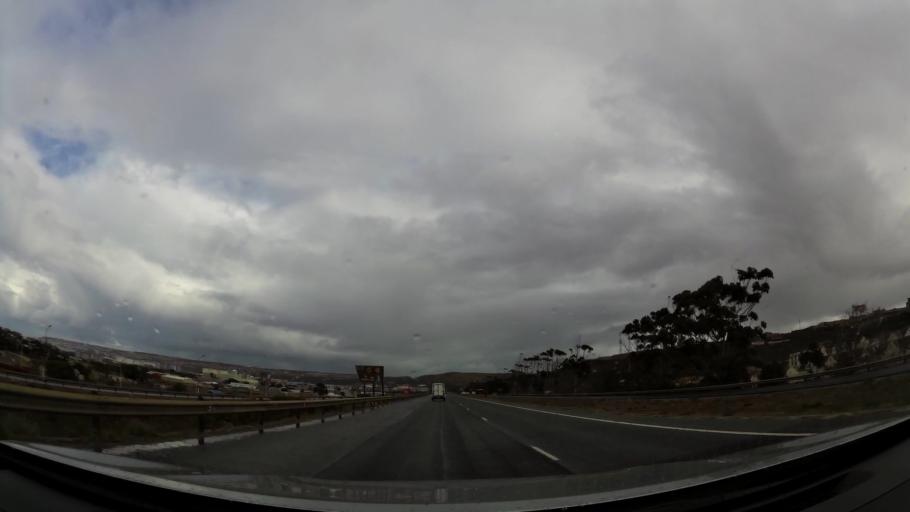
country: ZA
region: Western Cape
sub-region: Eden District Municipality
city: Mossel Bay
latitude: -34.1364
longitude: 22.1015
